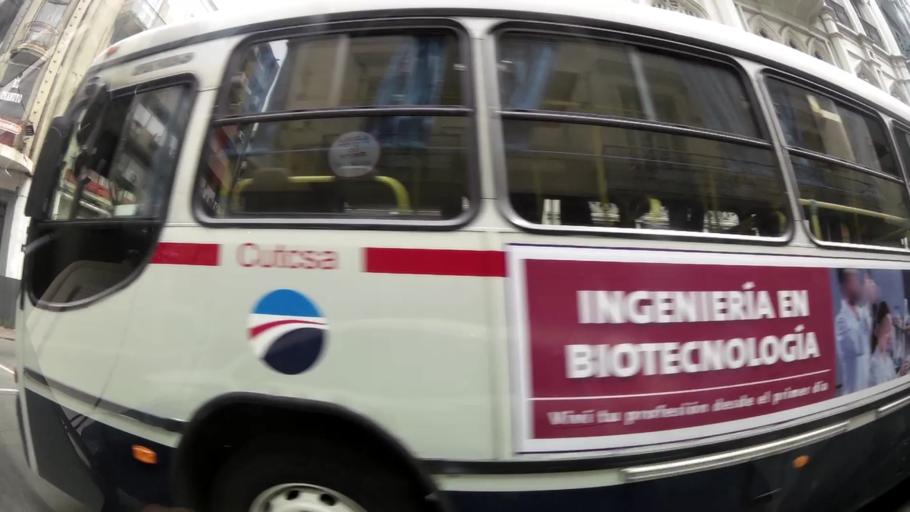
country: UY
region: Montevideo
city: Montevideo
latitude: -34.9051
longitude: -56.2038
